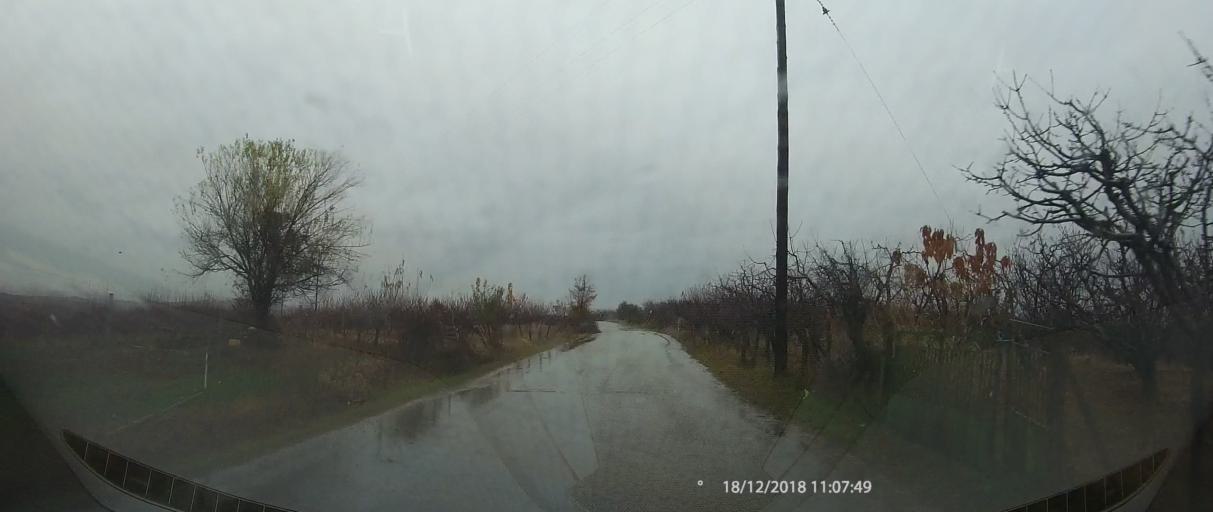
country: GR
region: Central Macedonia
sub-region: Nomos Pierias
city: Kato Milia
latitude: 40.2255
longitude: 22.3397
